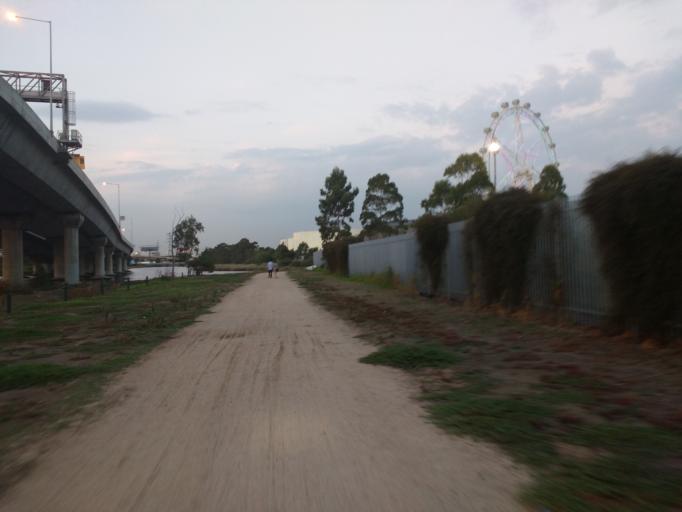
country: AU
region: Victoria
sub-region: Melbourne
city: Docklands
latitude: -37.8148
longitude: 144.9342
